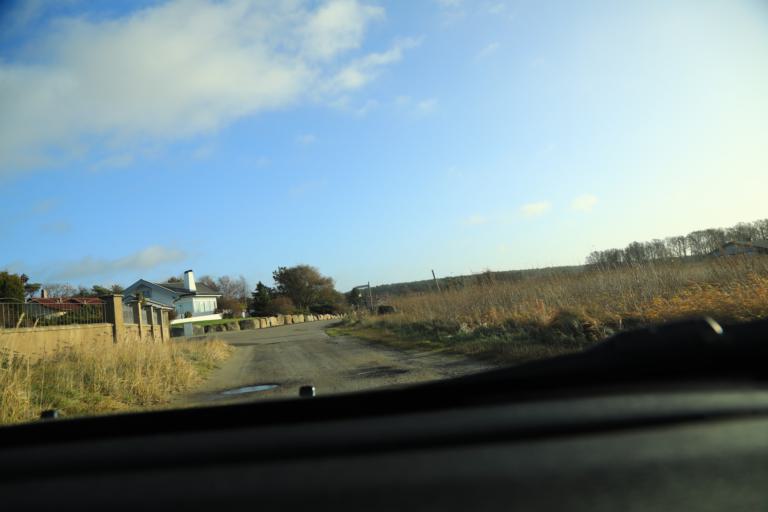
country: SE
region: Halland
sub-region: Varbergs Kommun
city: Varberg
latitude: 57.1849
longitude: 12.2147
